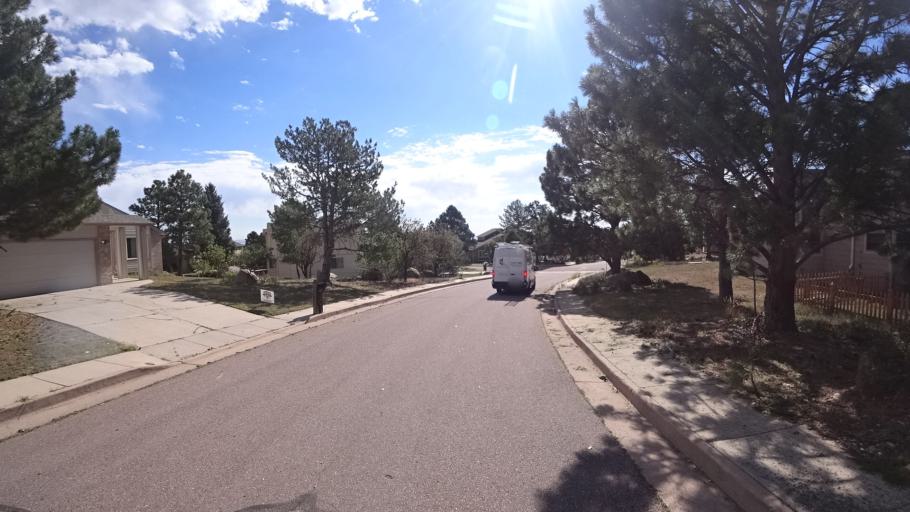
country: US
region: Colorado
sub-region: El Paso County
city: Fort Carson
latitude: 38.7620
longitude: -104.8283
